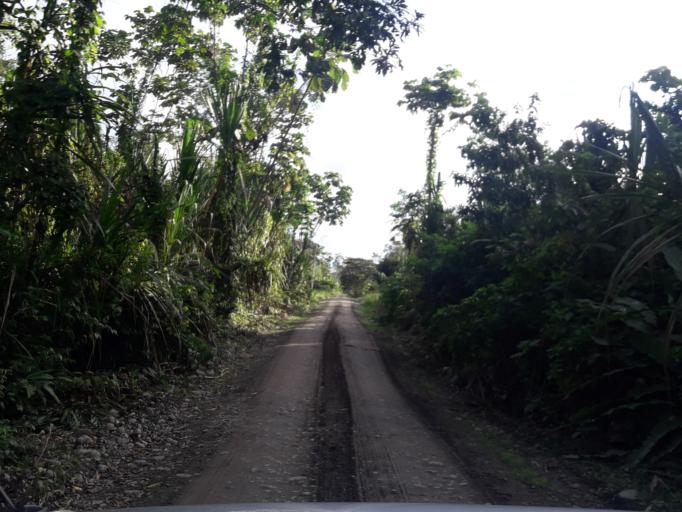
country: EC
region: Orellana
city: Boca Suno
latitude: -0.8818
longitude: -77.2816
